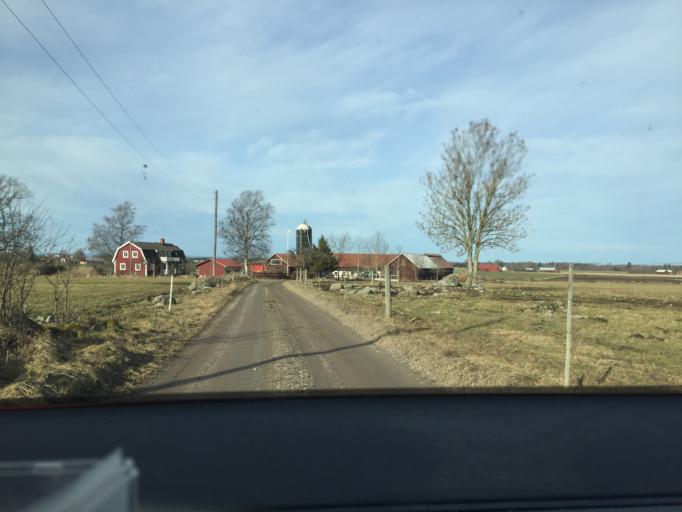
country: SE
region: OErebro
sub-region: Hallsbergs Kommun
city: Skollersta
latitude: 59.1243
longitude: 15.4327
